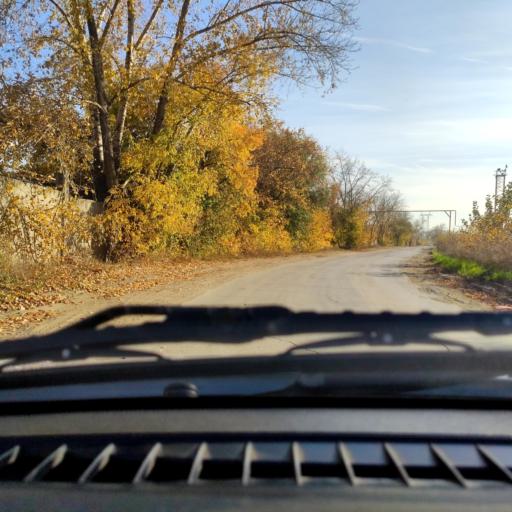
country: RU
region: Samara
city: Zhigulevsk
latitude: 53.4742
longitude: 49.5012
